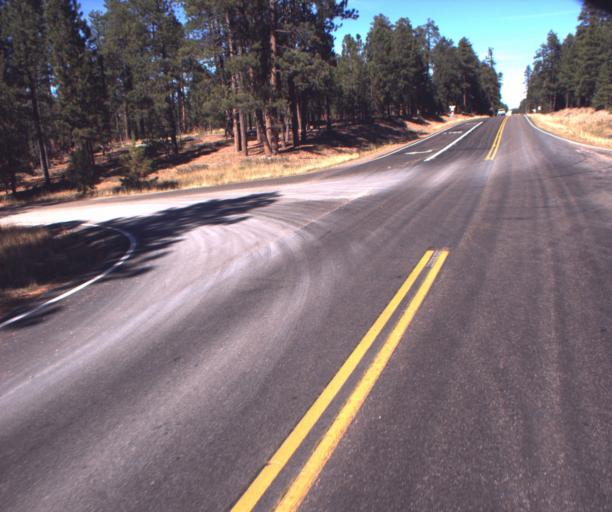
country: US
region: Arizona
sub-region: Coconino County
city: Fredonia
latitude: 36.7090
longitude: -112.2179
